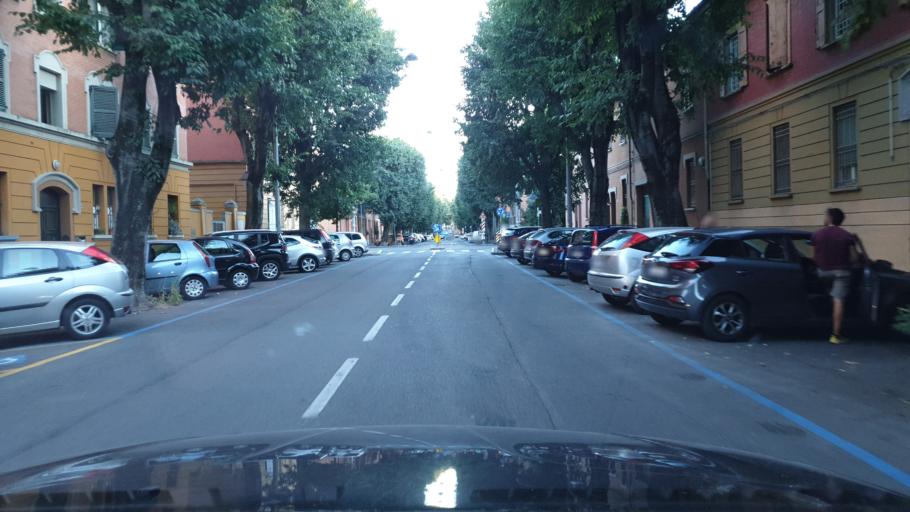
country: IT
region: Emilia-Romagna
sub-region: Provincia di Bologna
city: Bologna
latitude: 44.4958
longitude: 11.3626
